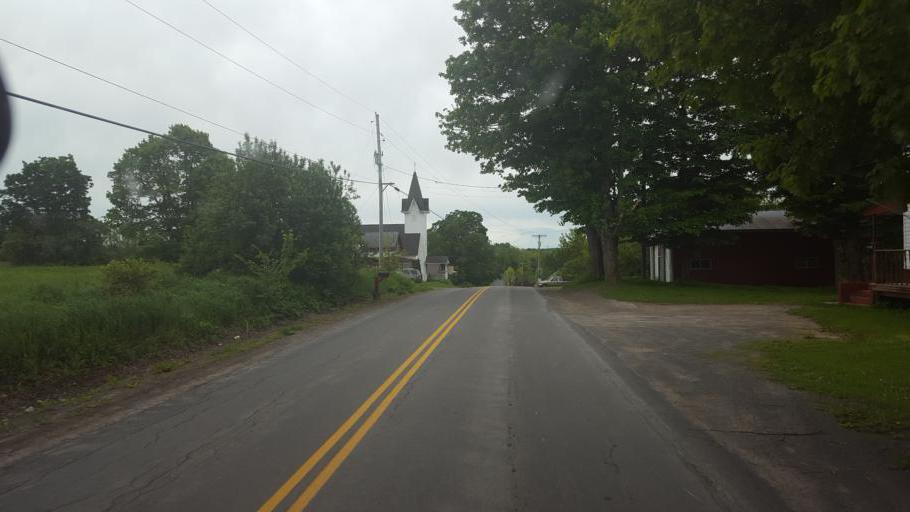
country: US
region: New York
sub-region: Herkimer County
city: Ilion
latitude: 42.9341
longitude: -75.0357
